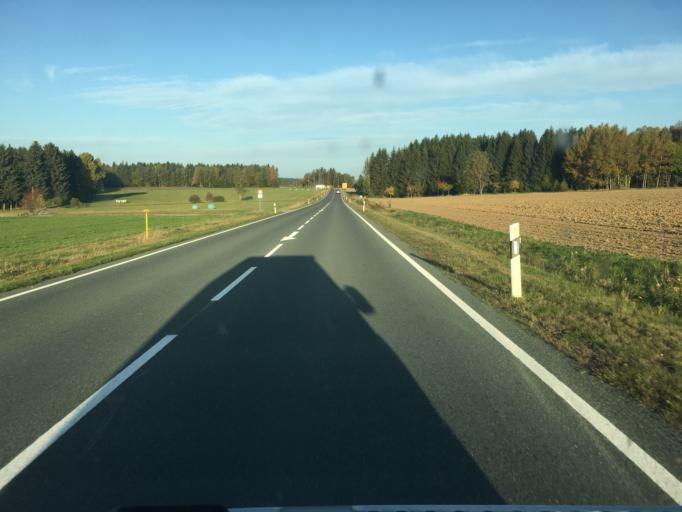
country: DE
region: Saxony
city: Schneeberg
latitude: 50.6072
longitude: 12.6007
